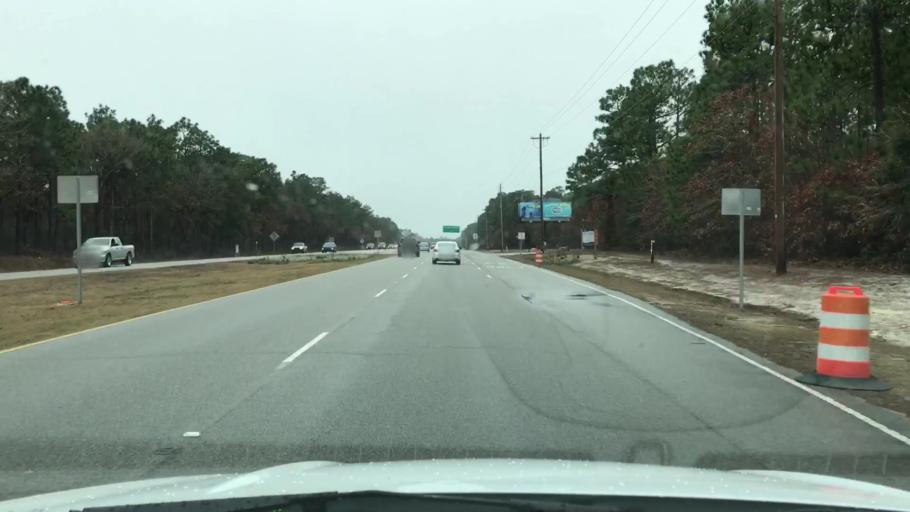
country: US
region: South Carolina
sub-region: Horry County
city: Myrtle Beach
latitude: 33.7514
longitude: -78.8312
